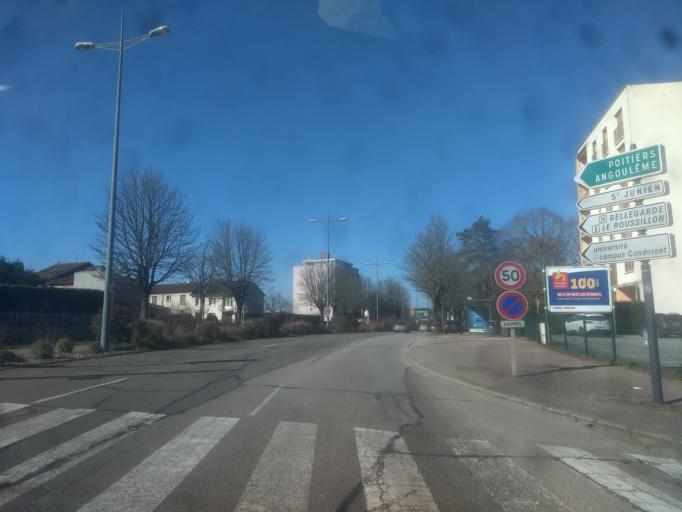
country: FR
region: Limousin
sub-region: Departement de la Haute-Vienne
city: Isle
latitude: 45.8212
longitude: 1.2301
